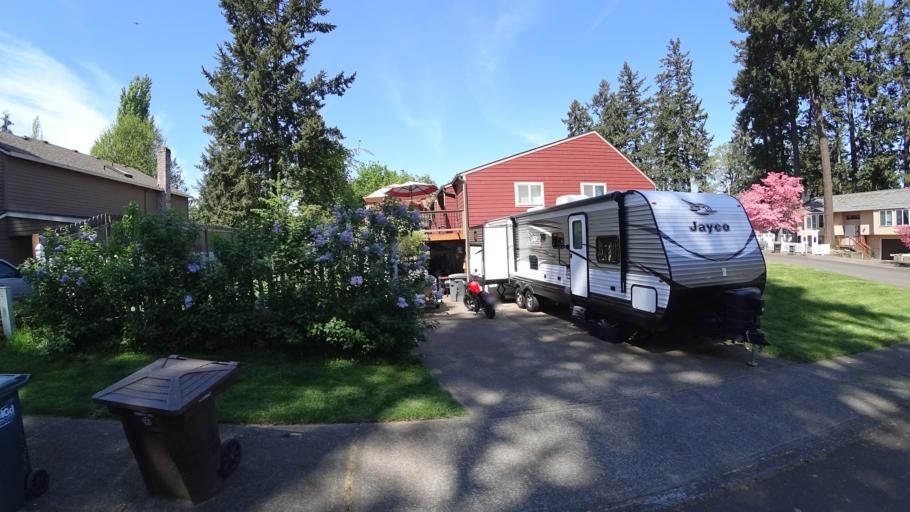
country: US
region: Oregon
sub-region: Washington County
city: Hillsboro
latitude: 45.5184
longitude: -122.9530
